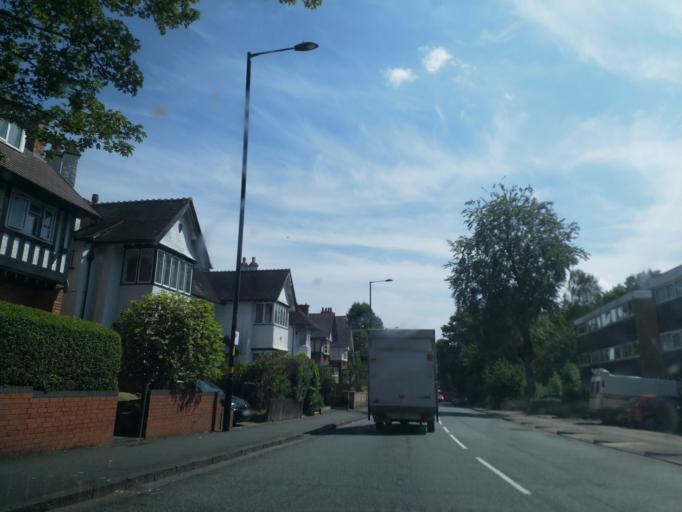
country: GB
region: England
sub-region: City and Borough of Birmingham
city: Hockley
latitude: 52.5132
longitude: -1.9255
